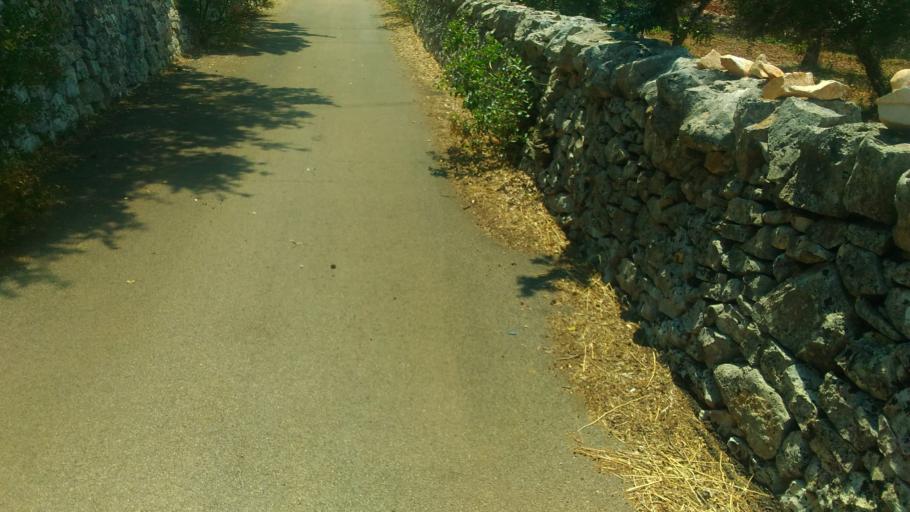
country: IT
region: Apulia
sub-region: Provincia di Brindisi
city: Cisternino
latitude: 40.7432
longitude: 17.3806
